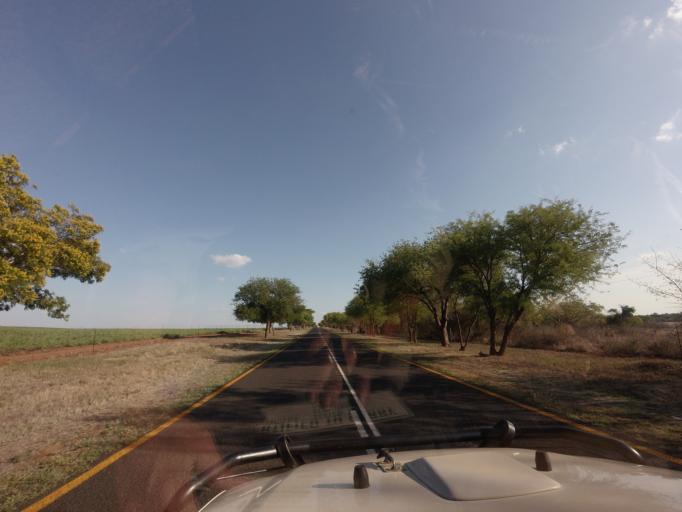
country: ZA
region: Mpumalanga
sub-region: Ehlanzeni District
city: Komatipoort
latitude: -25.3692
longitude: 31.9030
